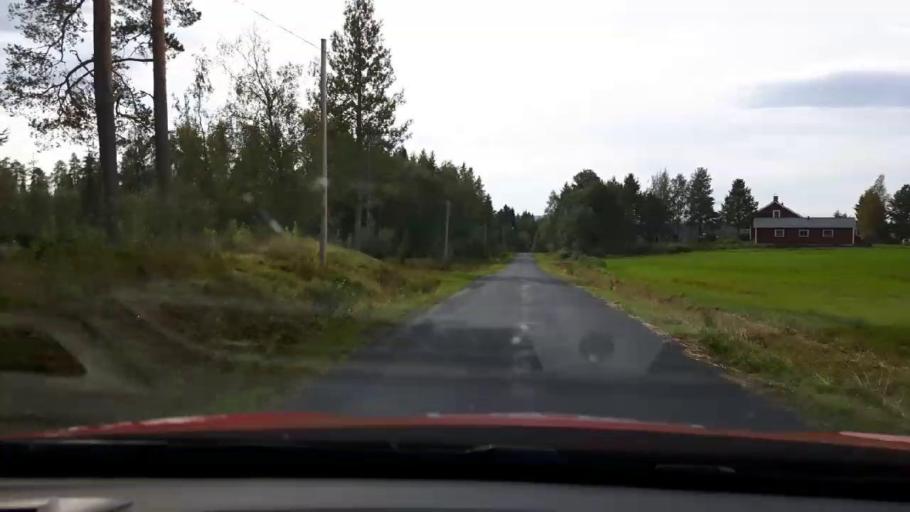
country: SE
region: Jaemtland
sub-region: Krokoms Kommun
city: Valla
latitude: 63.2672
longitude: 13.8530
